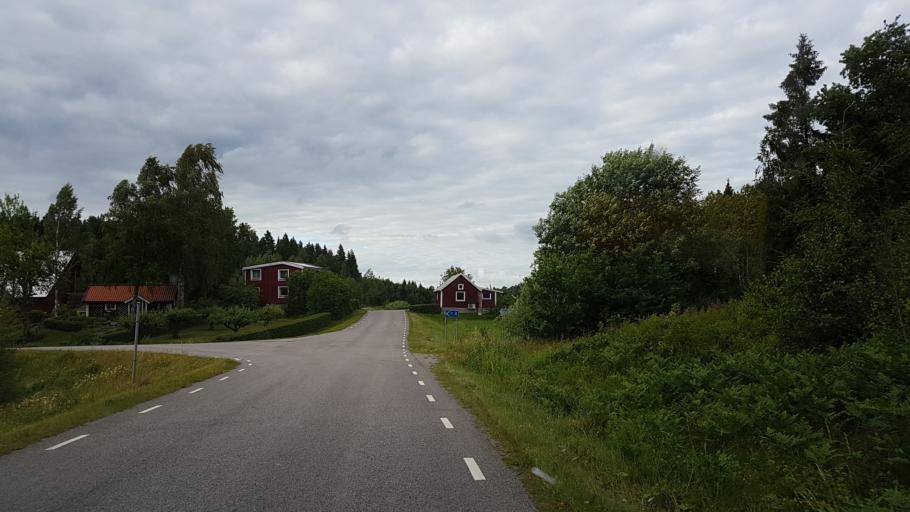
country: SE
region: OEstergoetland
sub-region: Valdemarsviks Kommun
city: Gusum
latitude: 58.4639
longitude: 16.5840
